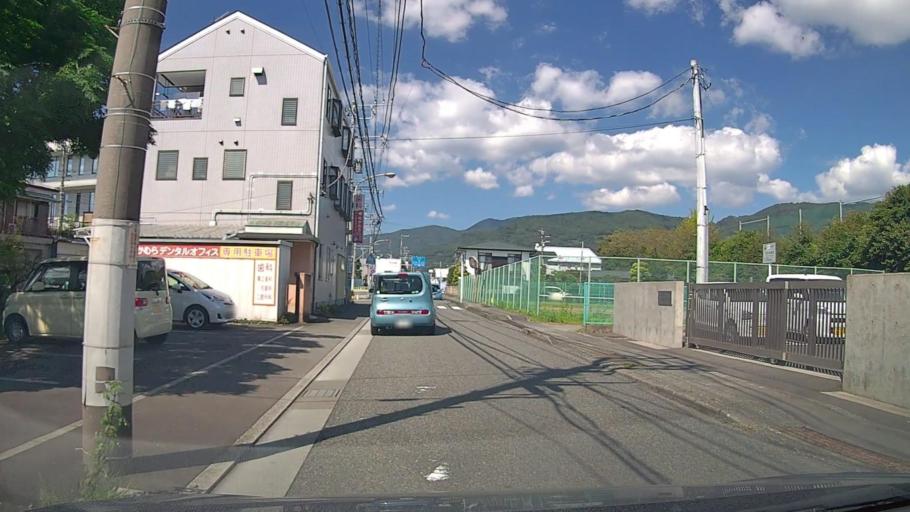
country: JP
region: Kanagawa
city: Odawara
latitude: 35.3354
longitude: 139.1242
